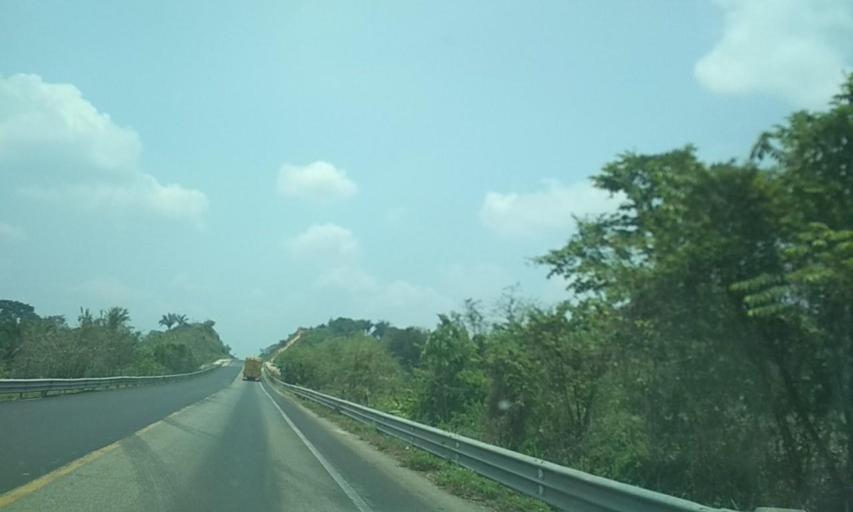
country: MX
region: Tabasco
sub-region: Huimanguillo
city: Francisco Rueda
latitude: 17.7243
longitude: -93.9590
